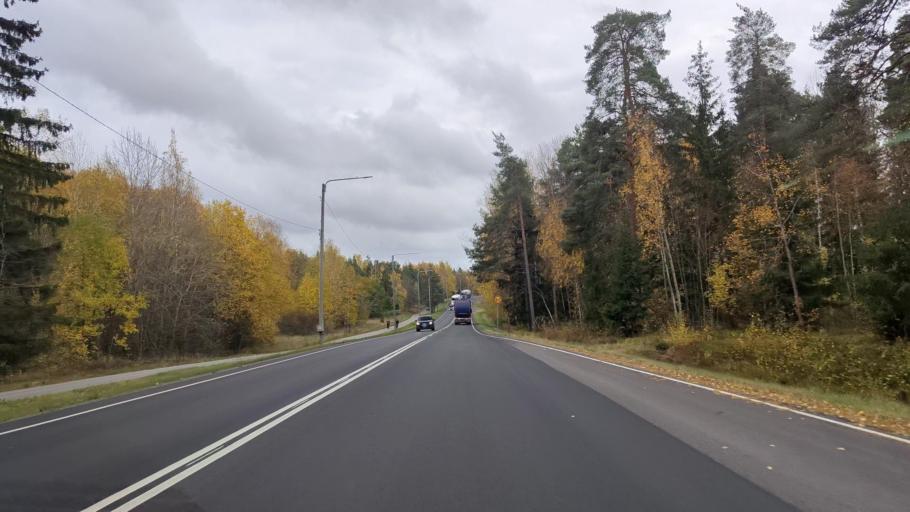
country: FI
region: Varsinais-Suomi
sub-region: Turku
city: Kaarina
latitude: 60.4548
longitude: 22.3683
